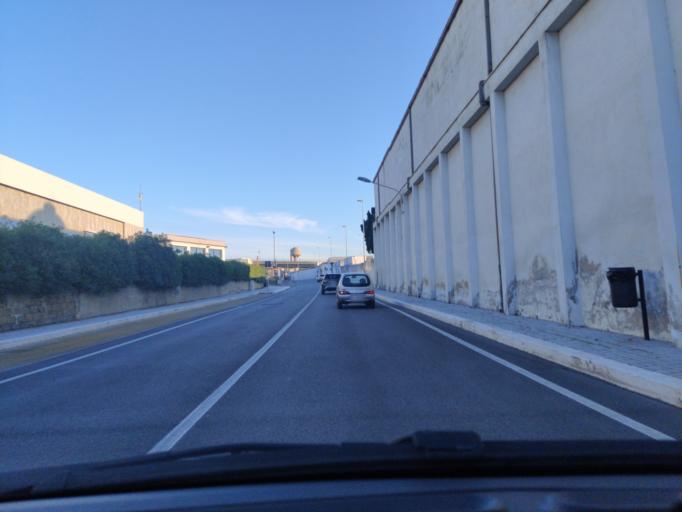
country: IT
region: Latium
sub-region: Citta metropolitana di Roma Capitale
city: Civitavecchia
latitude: 42.1058
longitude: 11.7832
